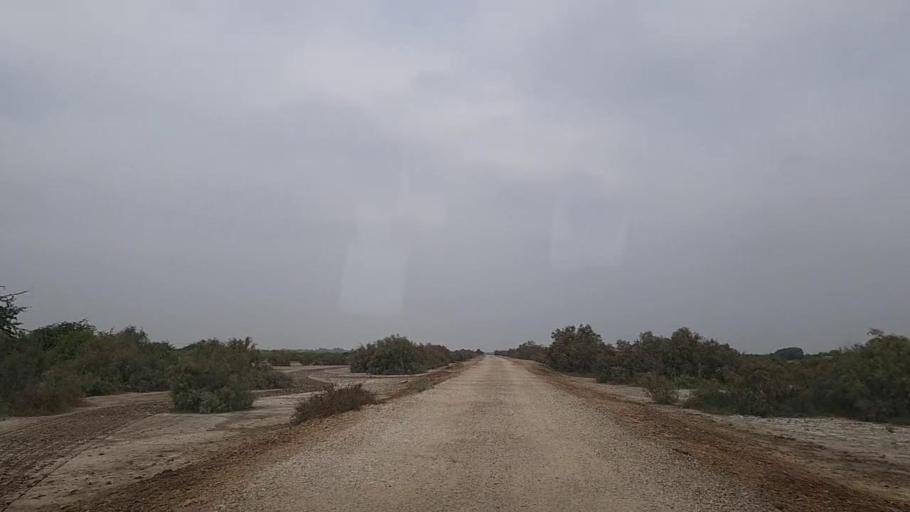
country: PK
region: Sindh
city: Mirpur Sakro
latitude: 24.6217
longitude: 67.7174
